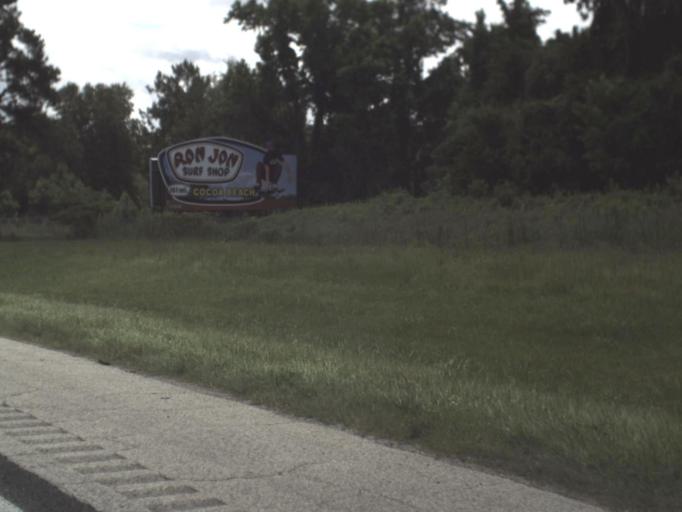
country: US
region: Florida
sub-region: Alachua County
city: Gainesville
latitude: 29.5958
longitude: -82.3679
